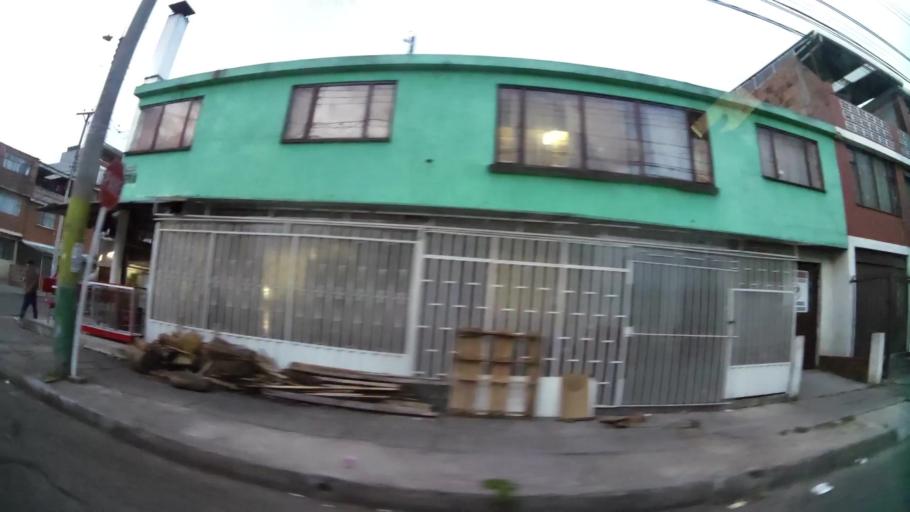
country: CO
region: Bogota D.C.
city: Bogota
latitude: 4.6067
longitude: -74.1285
